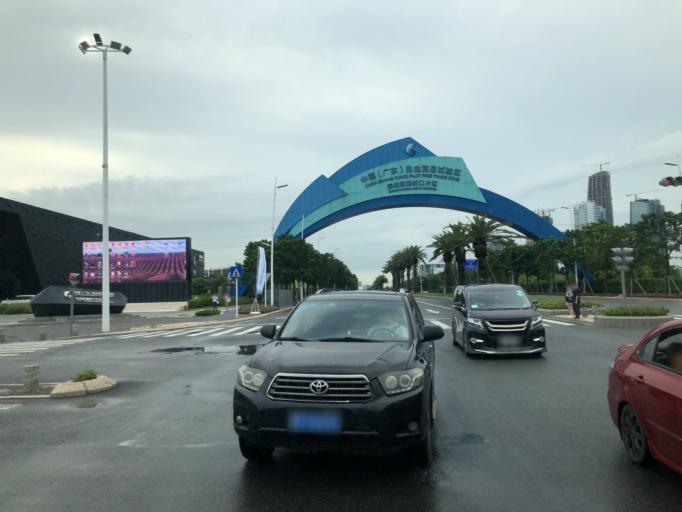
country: CN
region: Guangdong
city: Nantou
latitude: 22.5205
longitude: 113.8991
